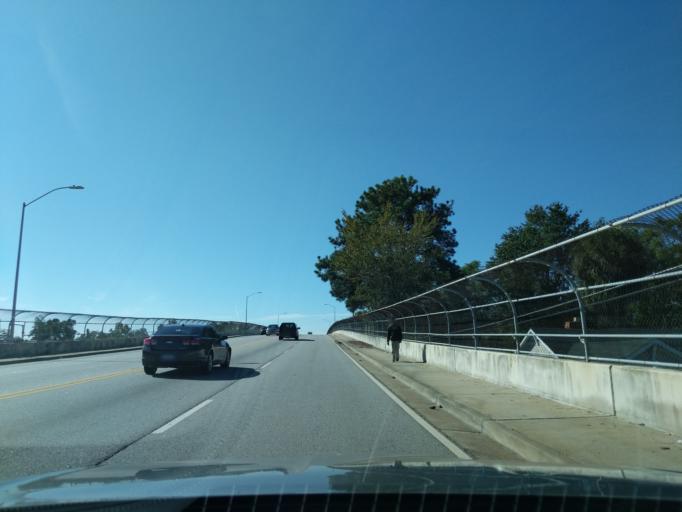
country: US
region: Georgia
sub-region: Richmond County
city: Augusta
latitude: 33.4663
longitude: -81.9938
